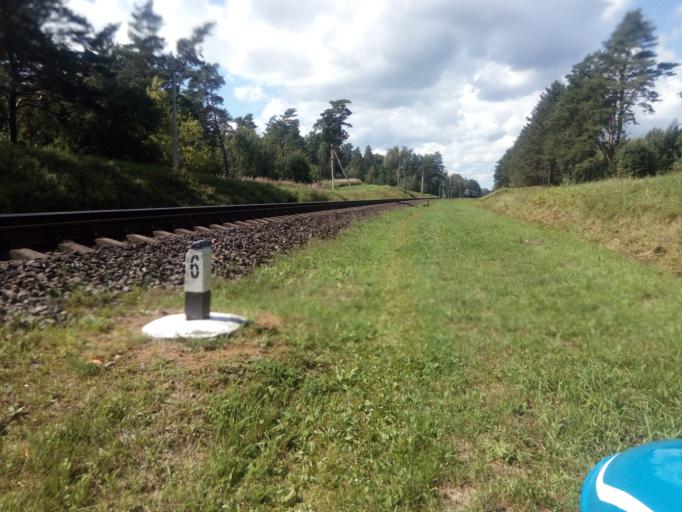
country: BY
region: Vitebsk
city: Dzisna
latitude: 55.6801
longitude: 28.2898
